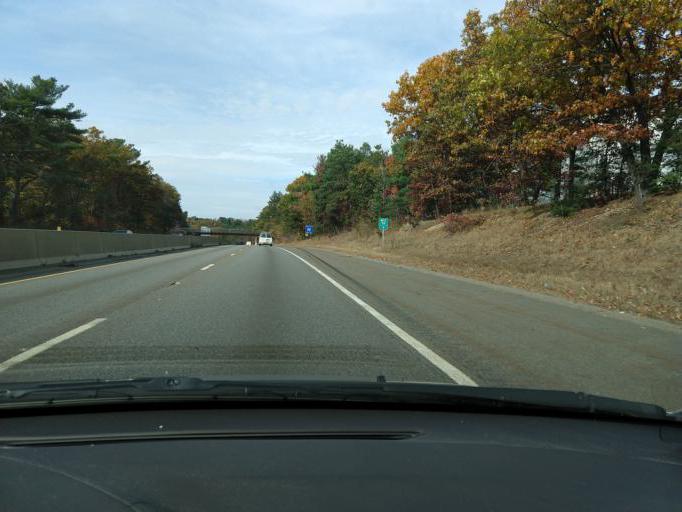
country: US
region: Massachusetts
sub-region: Worcester County
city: Leominster
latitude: 42.5444
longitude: -71.7548
